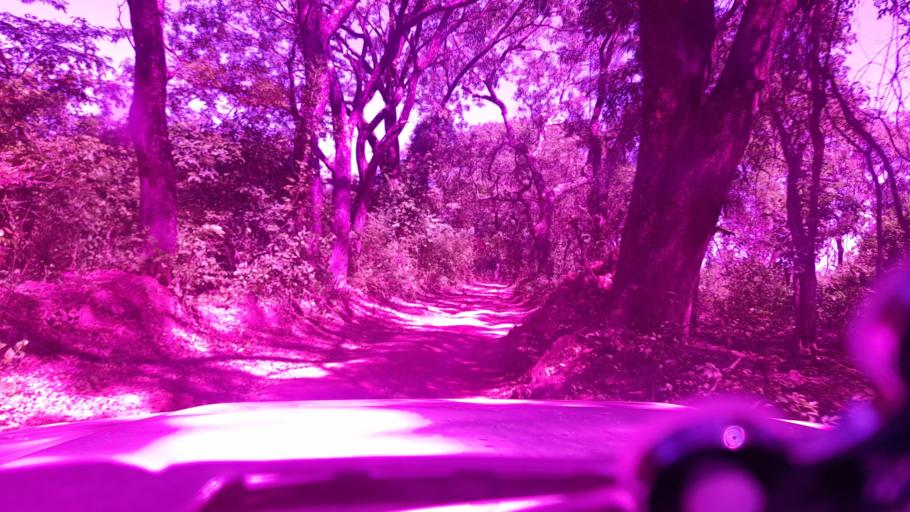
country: GW
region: Oio
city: Bissora
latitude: 12.4084
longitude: -15.5970
